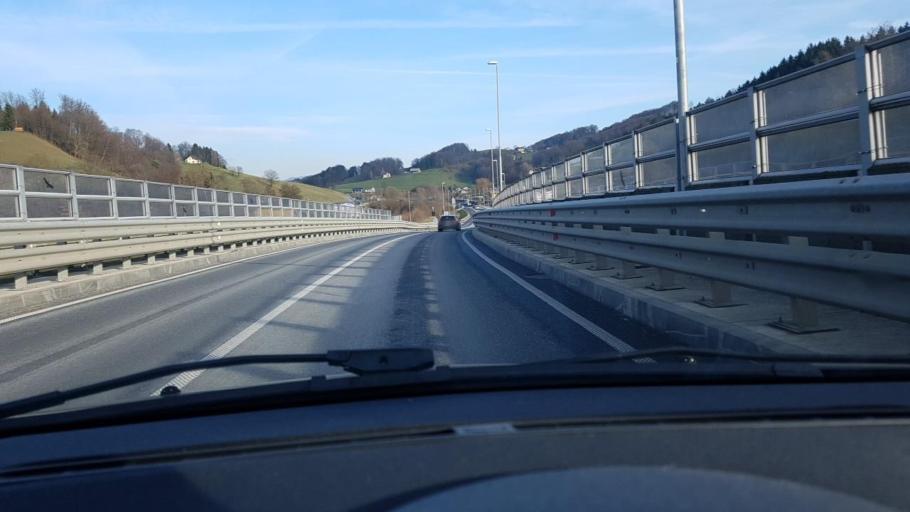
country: SI
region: Sentjur pri Celju
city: Sentjur
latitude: 46.2144
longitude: 15.4412
